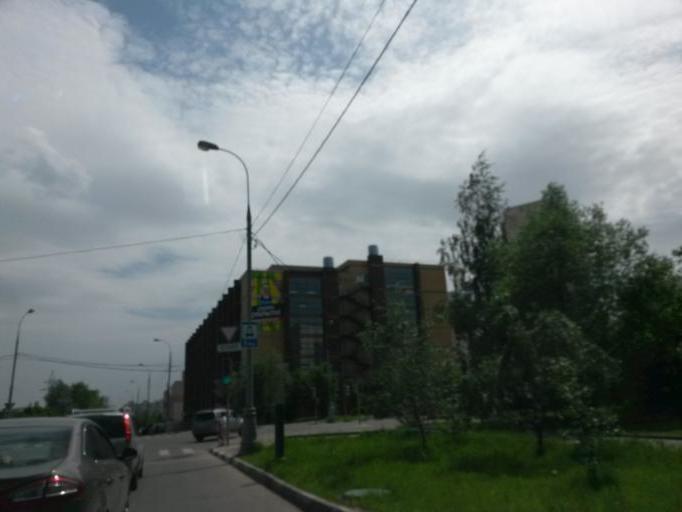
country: RU
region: Moskovskaya
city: Kommunarka
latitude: 55.5451
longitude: 37.5249
